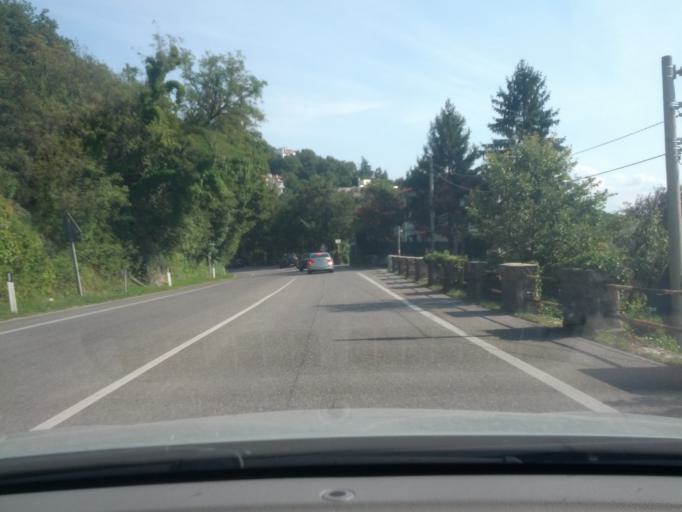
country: IT
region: Friuli Venezia Giulia
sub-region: Provincia di Trieste
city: Villa Opicina
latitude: 45.6752
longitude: 13.7891
